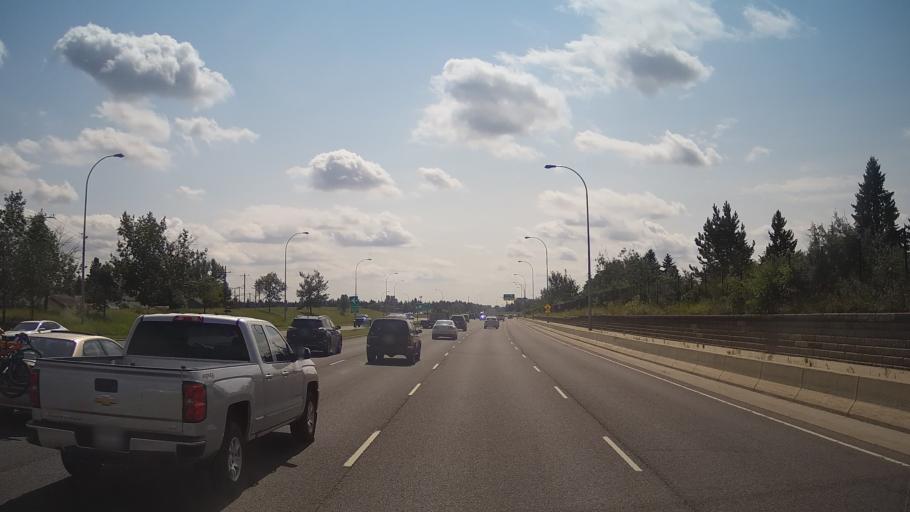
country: CA
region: Alberta
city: St. Albert
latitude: 53.5169
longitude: -113.6155
